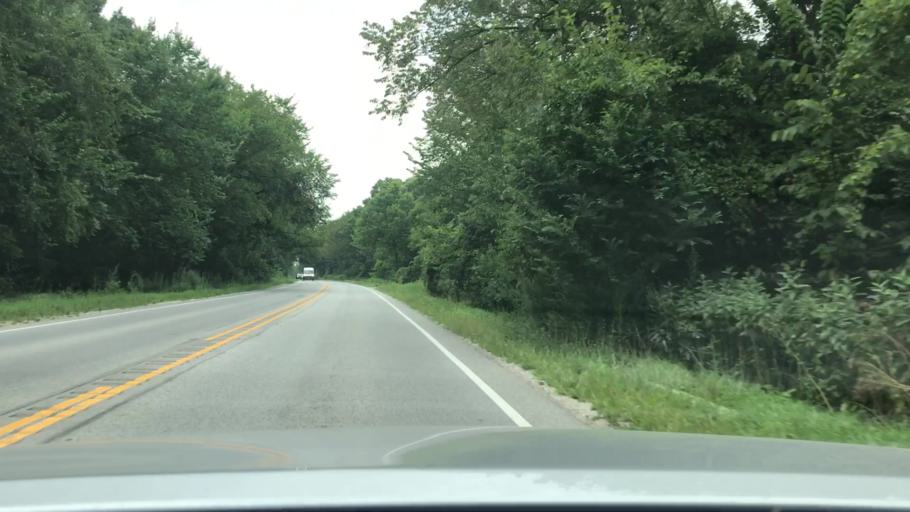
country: US
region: Illinois
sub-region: Cook County
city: Willow Springs
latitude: 41.6880
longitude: -87.8887
